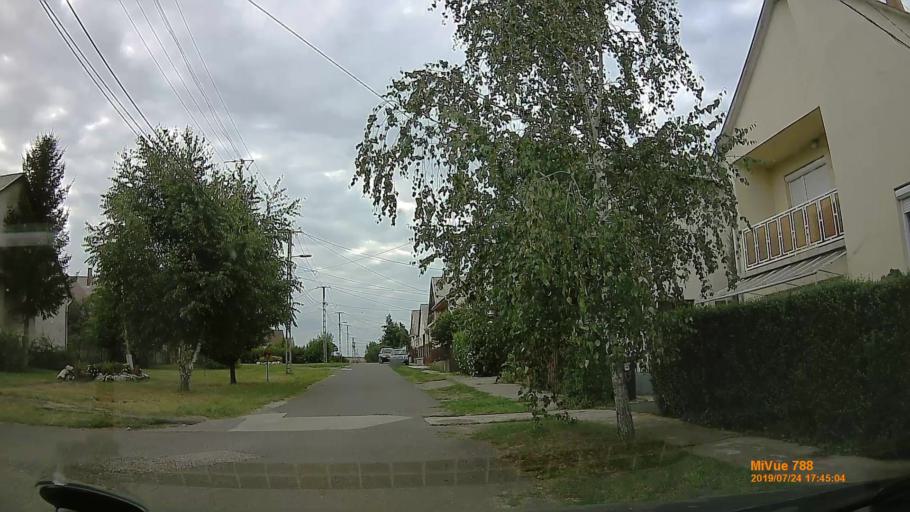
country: HU
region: Borsod-Abauj-Zemplen
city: Encs
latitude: 48.3369
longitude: 21.1048
